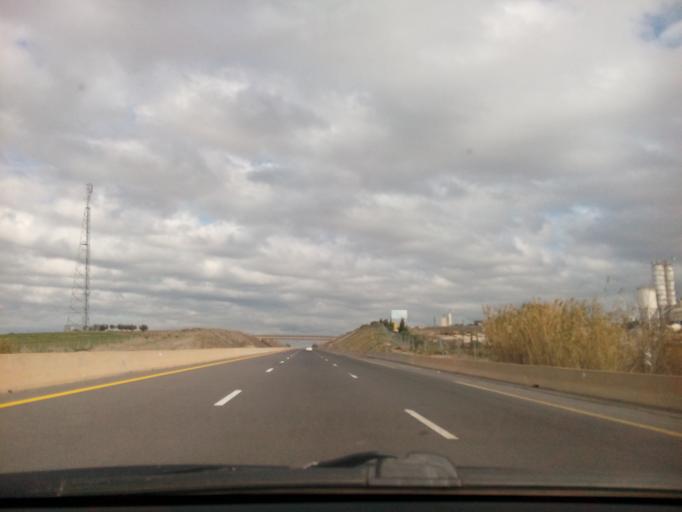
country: DZ
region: Tlemcen
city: Chetouane
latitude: 34.9665
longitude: -1.2673
